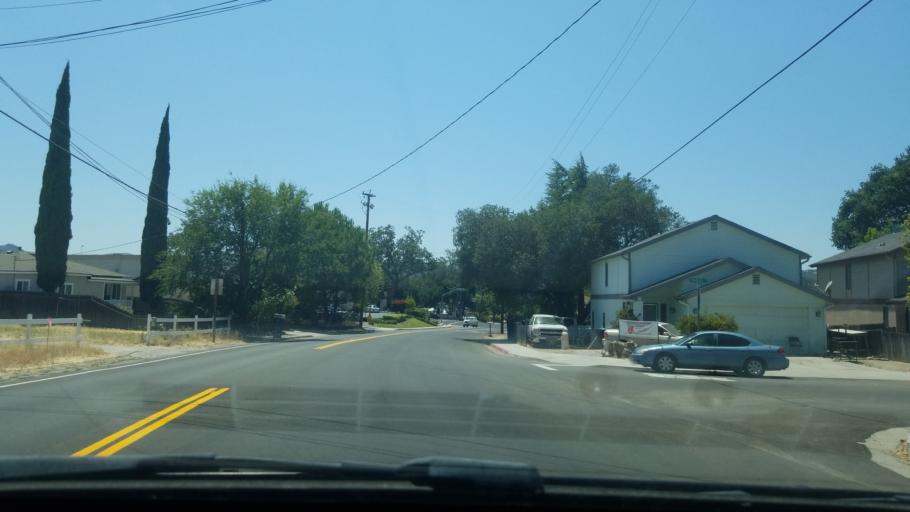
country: US
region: California
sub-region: San Luis Obispo County
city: Atascadero
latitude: 35.4784
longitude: -120.6549
